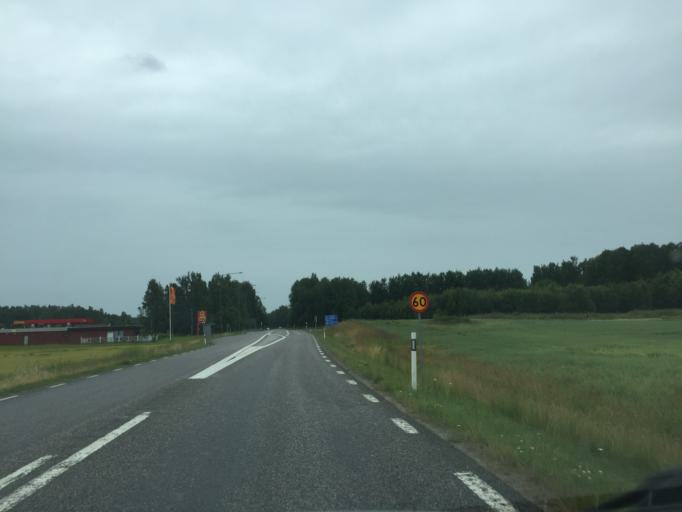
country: SE
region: OErebro
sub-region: Kumla Kommun
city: Hallabrottet
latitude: 59.1672
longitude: 15.2631
